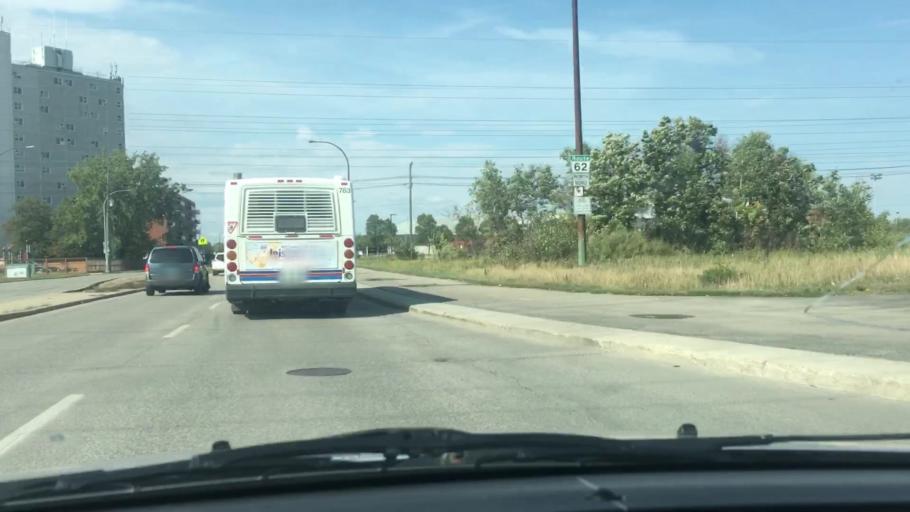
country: CA
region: Manitoba
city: Winnipeg
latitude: 49.8330
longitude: -97.1089
